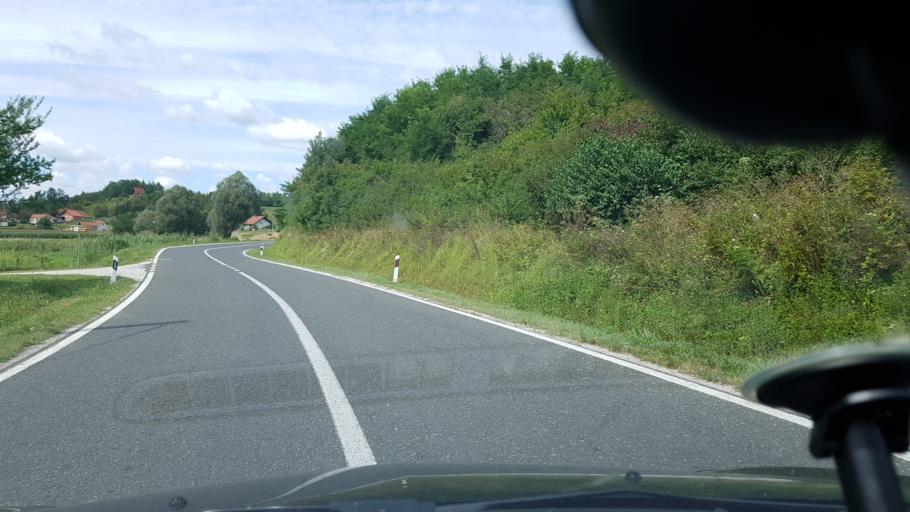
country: HR
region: Varazdinska
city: Lepoglava
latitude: 46.2104
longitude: 16.0206
